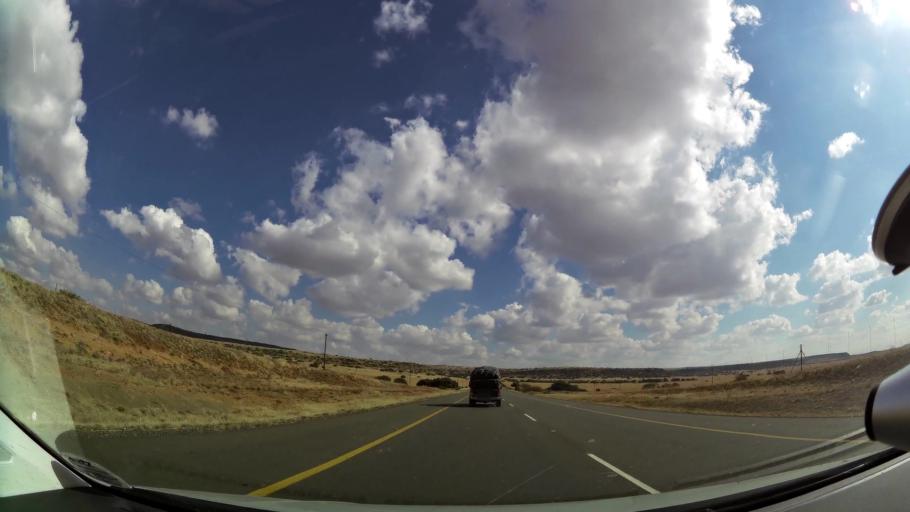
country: ZA
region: Orange Free State
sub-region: Mangaung Metropolitan Municipality
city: Bloemfontein
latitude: -29.1470
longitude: 26.0736
